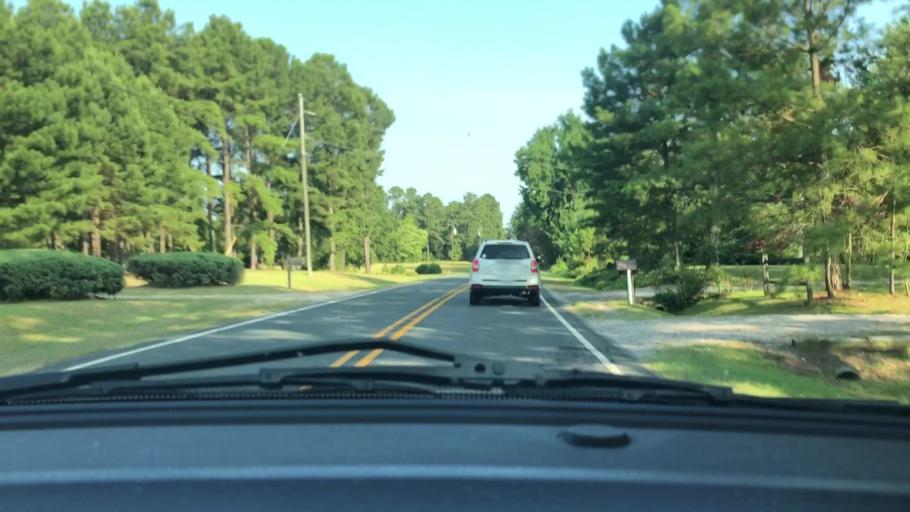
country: US
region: North Carolina
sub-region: Lee County
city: Broadway
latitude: 35.3726
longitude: -79.1001
